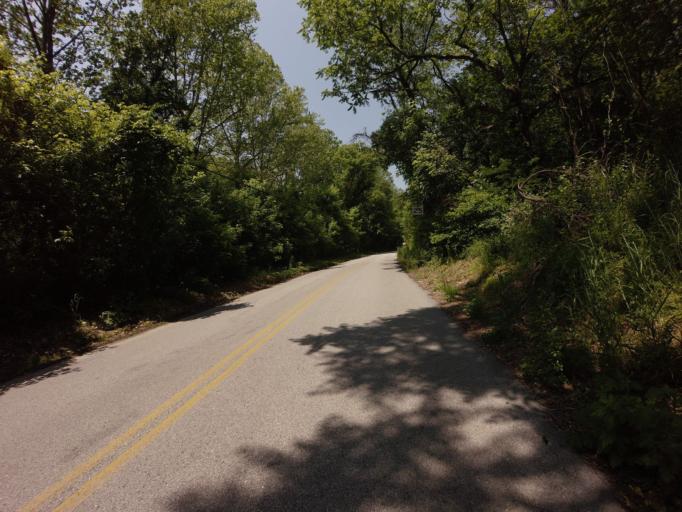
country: US
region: Maryland
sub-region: Howard County
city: Ilchester
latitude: 39.2571
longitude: -76.7784
